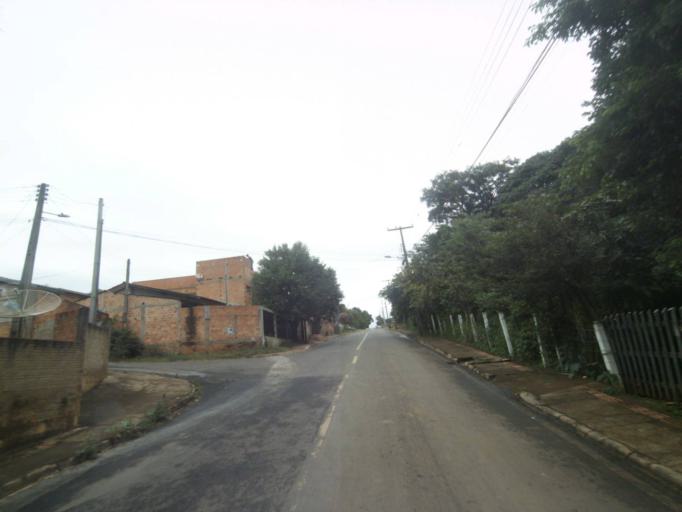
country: BR
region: Parana
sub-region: Telemaco Borba
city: Telemaco Borba
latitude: -24.3207
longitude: -50.6542
